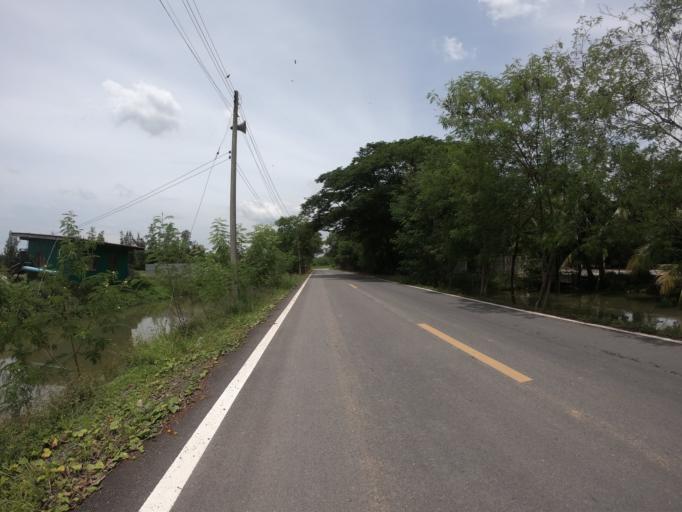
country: TH
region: Pathum Thani
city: Ban Lam Luk Ka
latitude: 14.0104
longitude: 100.8458
